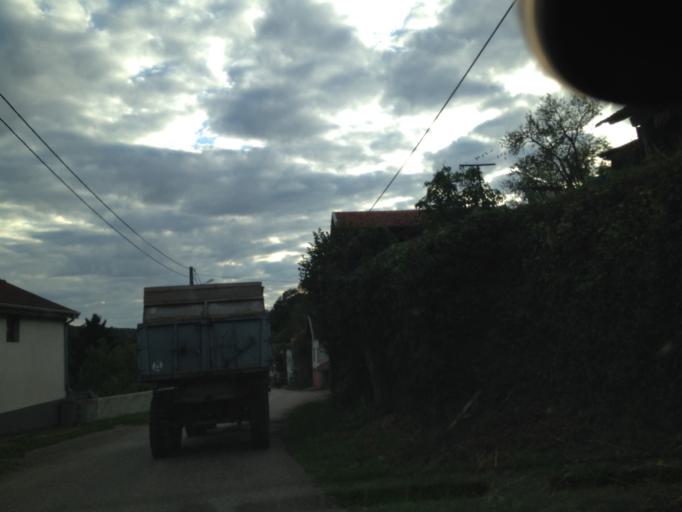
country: FR
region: Lorraine
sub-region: Departement des Vosges
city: Bains-les-Bains
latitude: 47.9786
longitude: 6.2050
